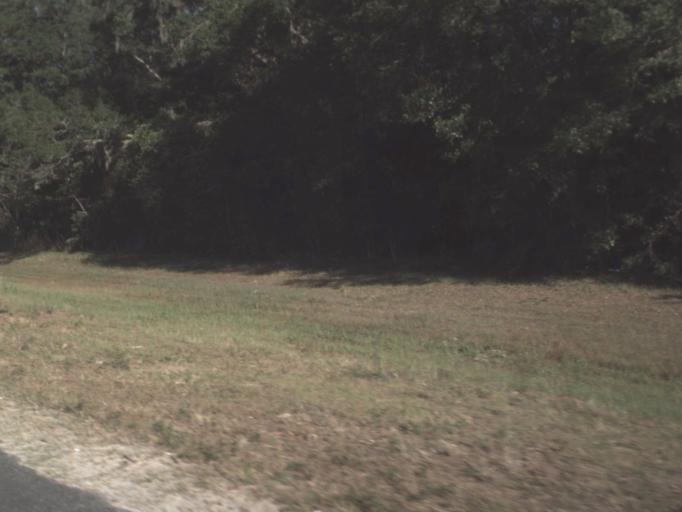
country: US
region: Florida
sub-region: Marion County
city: Ocala
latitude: 29.1864
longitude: -82.2449
